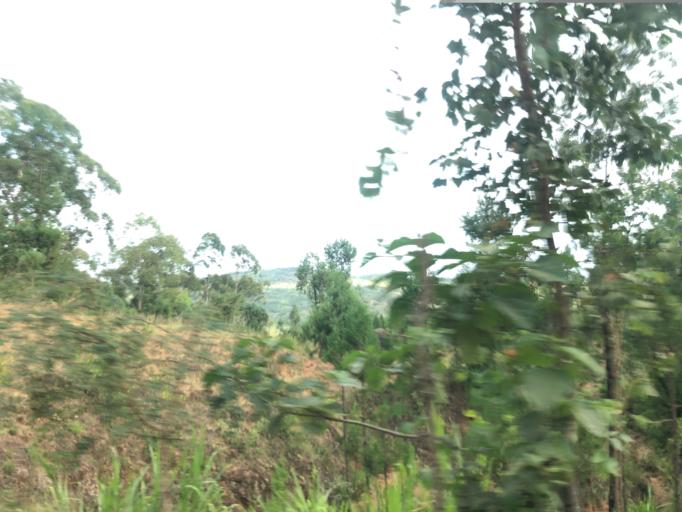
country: ET
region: Southern Nations, Nationalities, and People's Region
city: Konso
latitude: 5.2803
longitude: 37.3449
